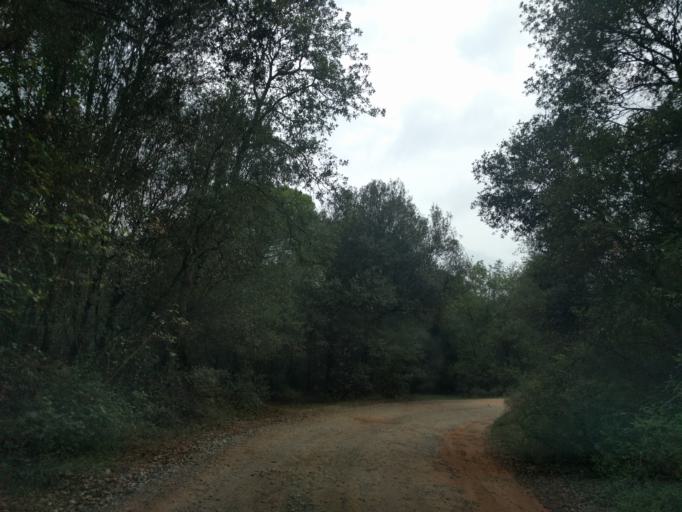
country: ES
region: Catalonia
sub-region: Provincia de Girona
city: la Cellera de Ter
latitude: 42.0038
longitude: 2.6322
